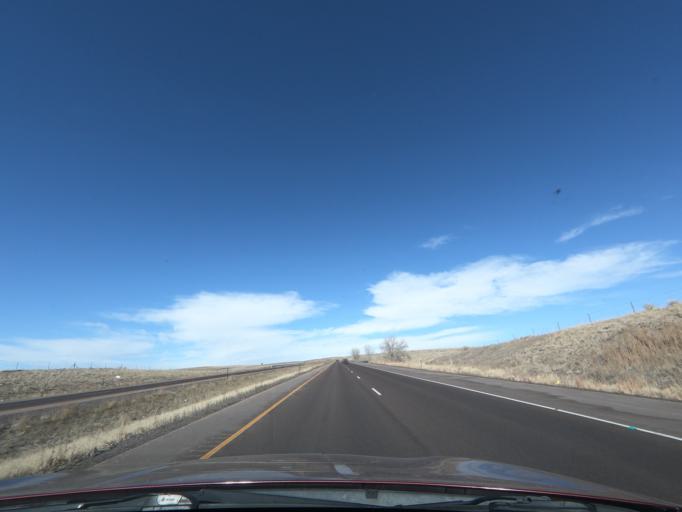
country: US
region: Colorado
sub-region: El Paso County
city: Security-Widefield
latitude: 38.7538
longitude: -104.6827
